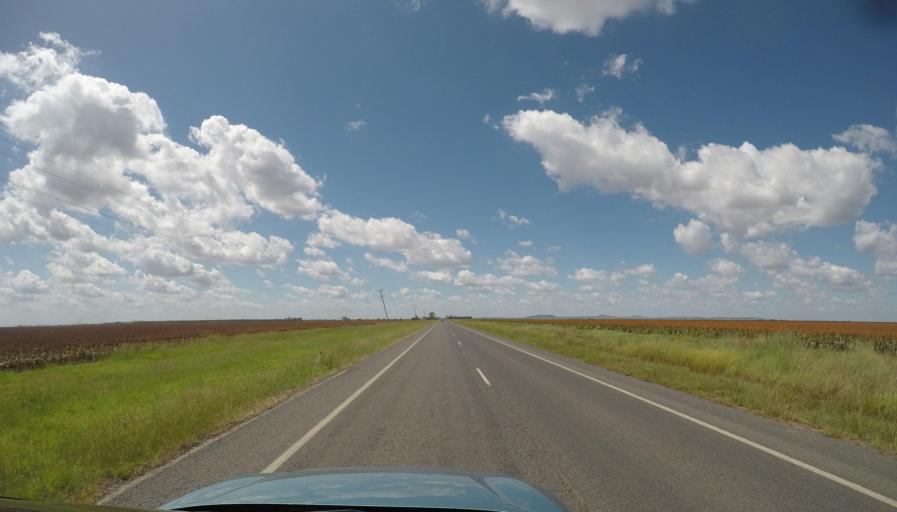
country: AU
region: Queensland
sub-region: Toowoomba
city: Oakey
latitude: -27.5172
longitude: 151.4076
